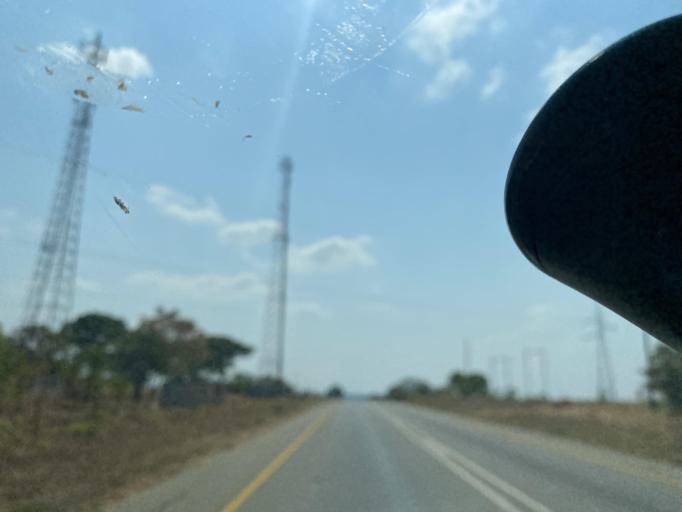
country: ZM
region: Lusaka
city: Chongwe
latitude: -15.5306
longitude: 28.6326
